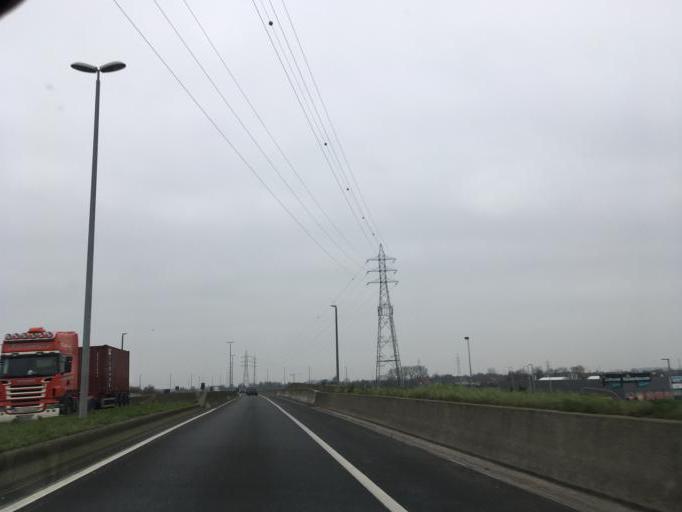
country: BE
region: Flanders
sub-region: Provincie West-Vlaanderen
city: Waregem
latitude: 50.8973
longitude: 3.3991
